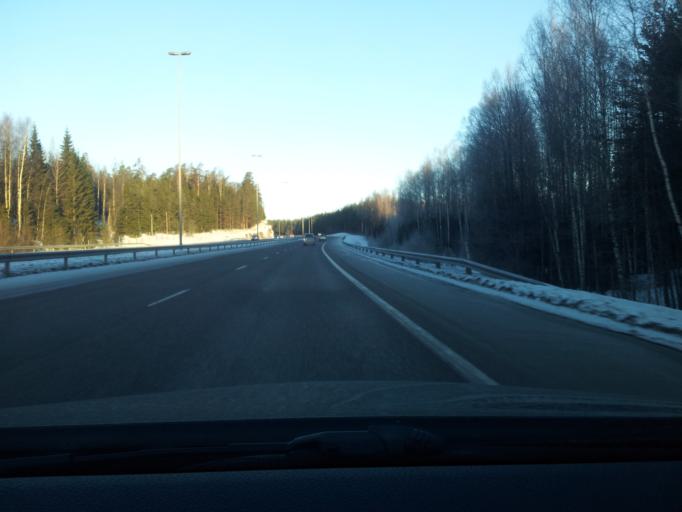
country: FI
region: Uusimaa
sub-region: Helsinki
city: Kirkkonummi
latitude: 60.2623
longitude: 24.4890
